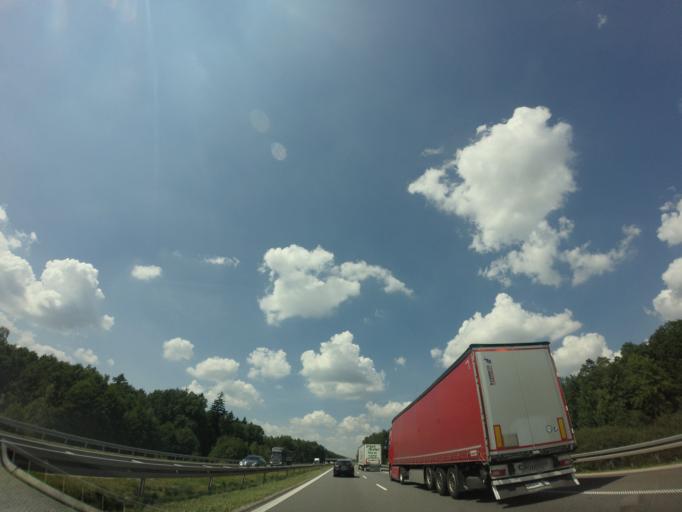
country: PL
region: Opole Voivodeship
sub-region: Powiat opolski
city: Proszkow
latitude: 50.5818
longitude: 17.8305
